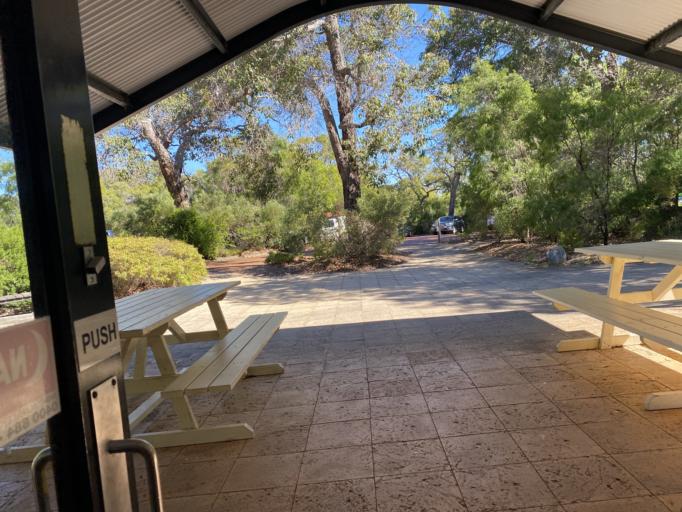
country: AU
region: Western Australia
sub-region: Augusta-Margaret River Shire
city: Margaret River
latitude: -34.0790
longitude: 115.0293
